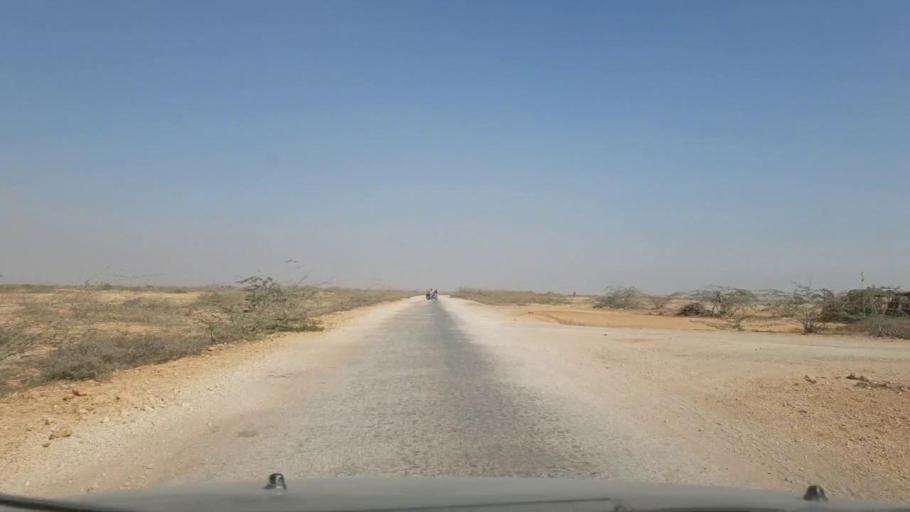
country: PK
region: Sindh
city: Thatta
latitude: 24.9014
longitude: 67.9216
